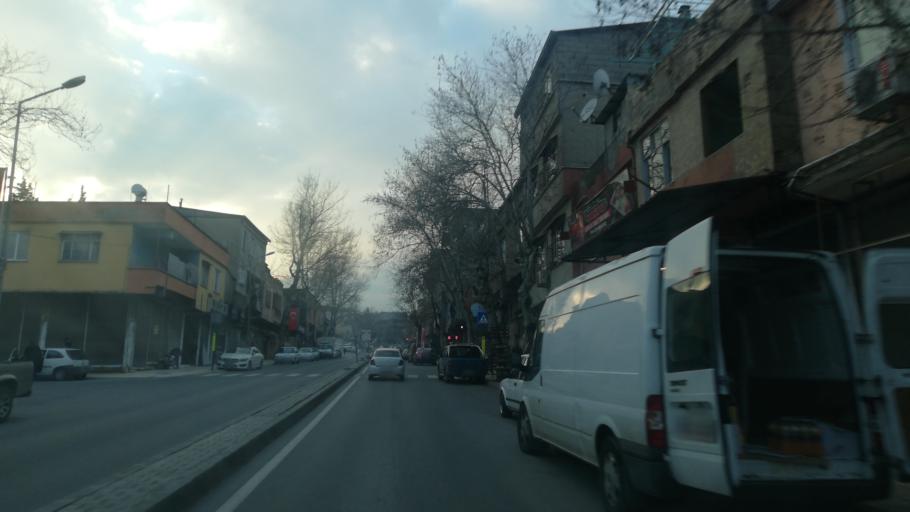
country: TR
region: Kahramanmaras
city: Kahramanmaras
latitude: 37.5887
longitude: 36.9155
